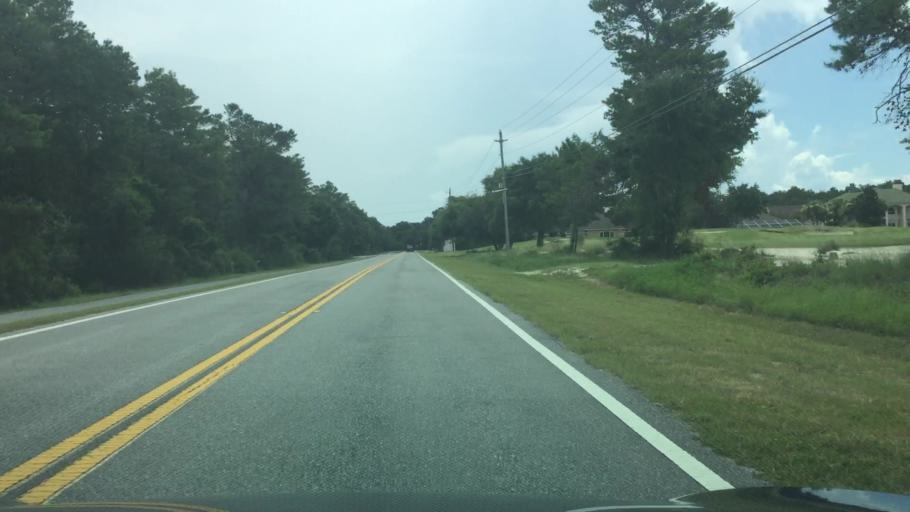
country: US
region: Florida
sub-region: Bay County
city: Upper Grand Lagoon
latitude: 30.1468
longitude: -85.7163
